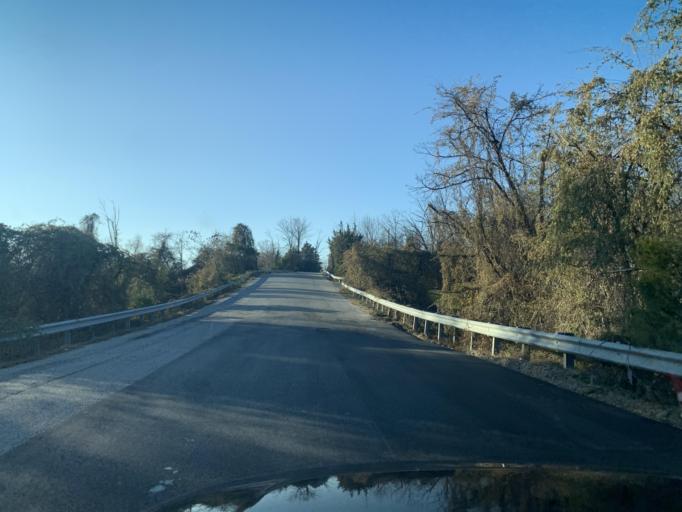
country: US
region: Maryland
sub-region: Baltimore County
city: Carney
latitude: 39.3840
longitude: -76.4961
